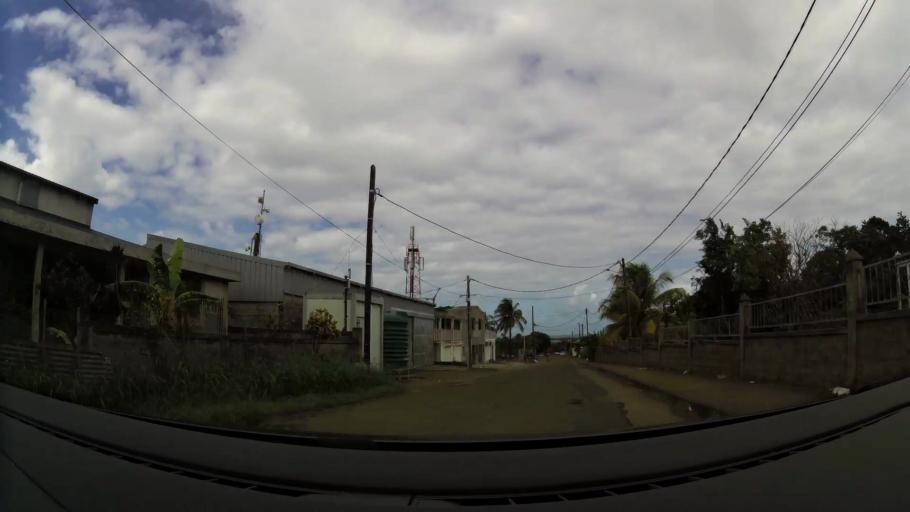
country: GP
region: Guadeloupe
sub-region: Guadeloupe
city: Sainte-Rose
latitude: 16.3261
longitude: -61.6941
